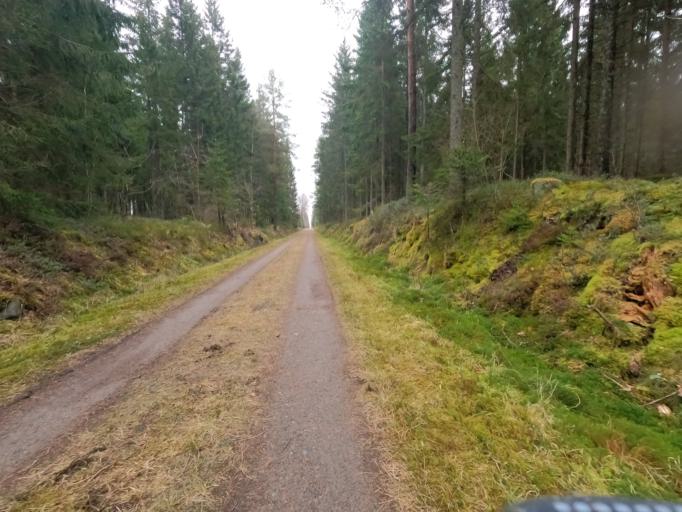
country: SE
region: Kronoberg
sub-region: Ljungby Kommun
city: Ljungby
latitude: 56.8255
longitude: 13.8837
